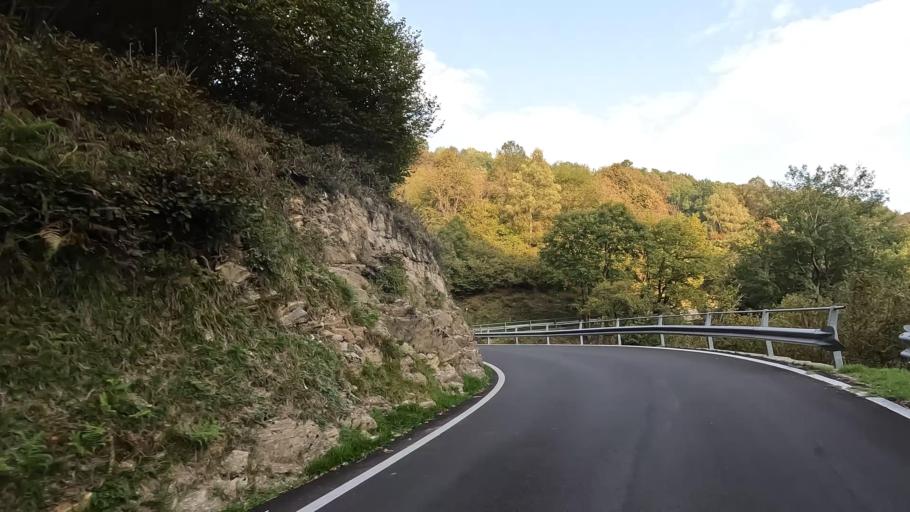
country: IT
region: Lombardy
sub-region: Provincia di Como
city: Blessagno
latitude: 45.9548
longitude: 9.1103
